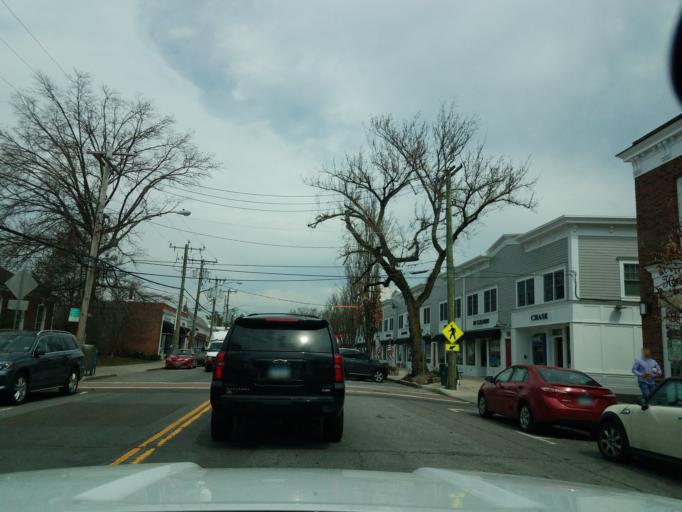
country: US
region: Connecticut
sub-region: Fairfield County
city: Old Greenwich
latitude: 41.0304
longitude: -73.5673
